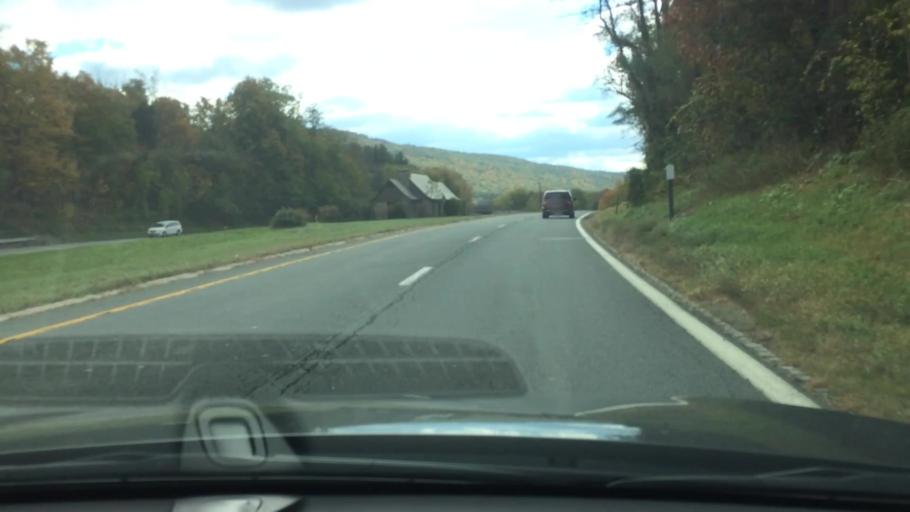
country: US
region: New York
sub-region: Dutchess County
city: Hillside Lake
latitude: 41.5487
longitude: -73.7749
